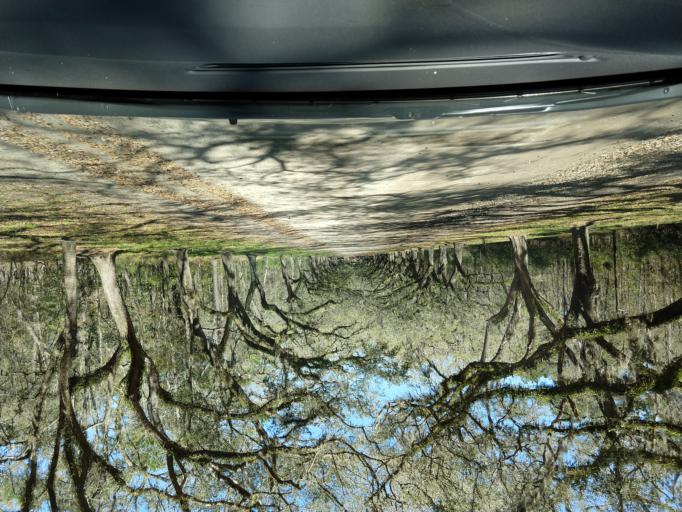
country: US
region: Georgia
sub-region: Chatham County
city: Isle of Hope
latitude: 31.9772
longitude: -81.0691
